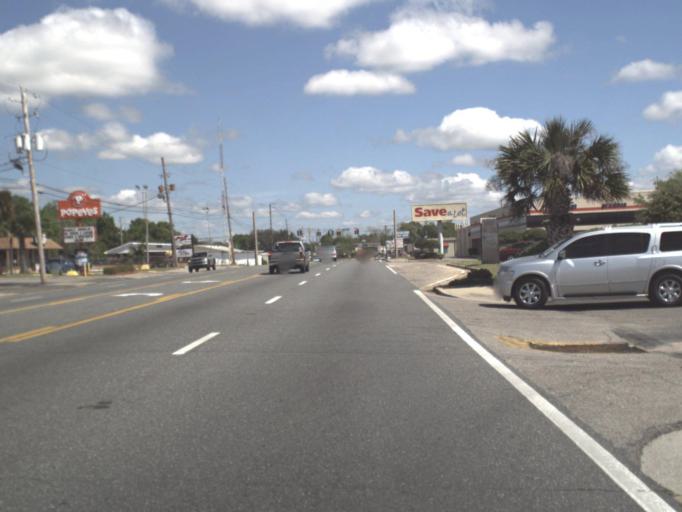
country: US
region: Florida
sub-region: Escambia County
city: Goulding
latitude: 30.4472
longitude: -87.2397
